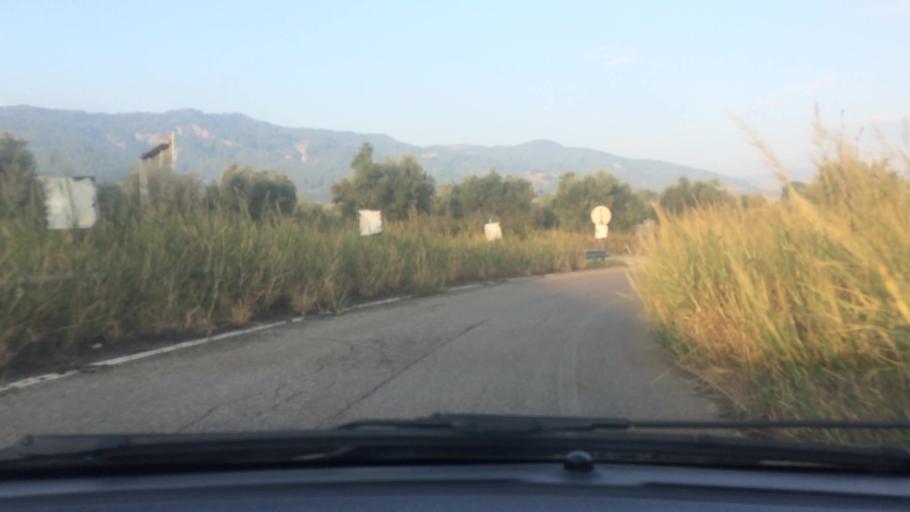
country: IT
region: Basilicate
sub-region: Provincia di Matera
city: Montescaglioso
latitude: 40.5266
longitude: 16.6263
